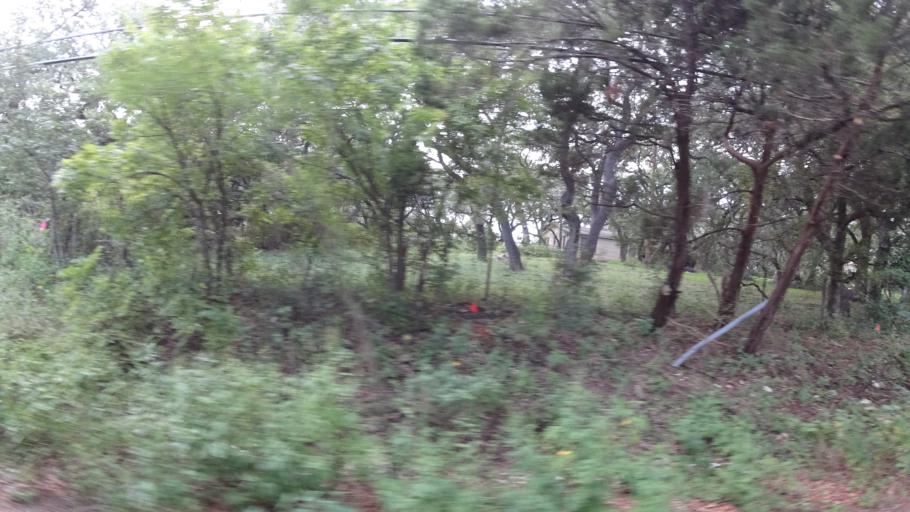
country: US
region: Texas
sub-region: Travis County
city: Onion Creek
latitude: 30.1922
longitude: -97.7943
